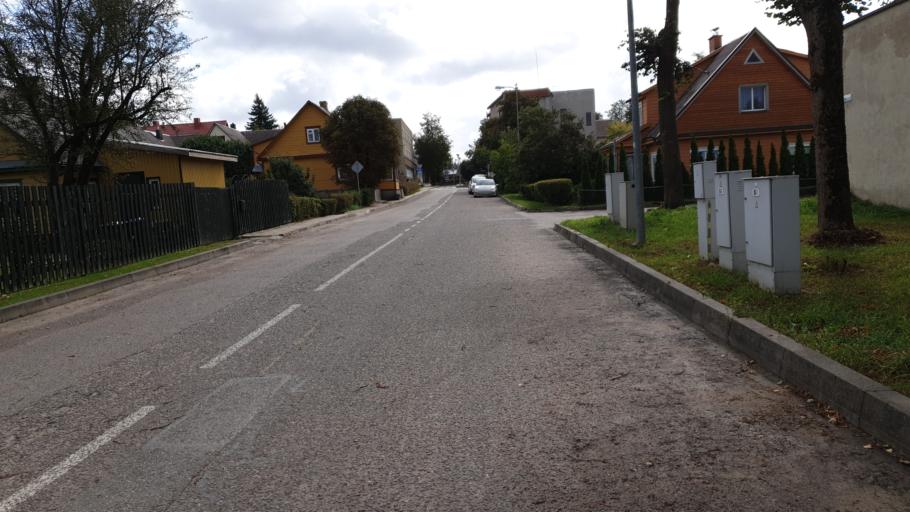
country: LT
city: Moletai
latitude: 55.2333
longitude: 25.4176
